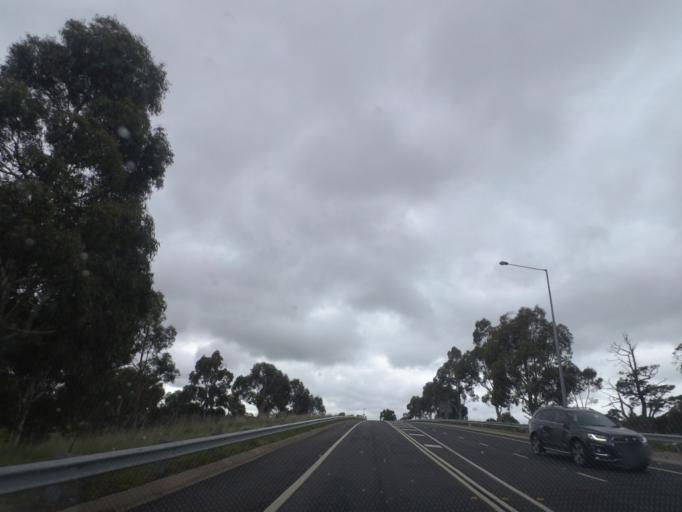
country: AU
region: Victoria
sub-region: Hume
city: Sunbury
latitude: -37.3217
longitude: 144.5250
